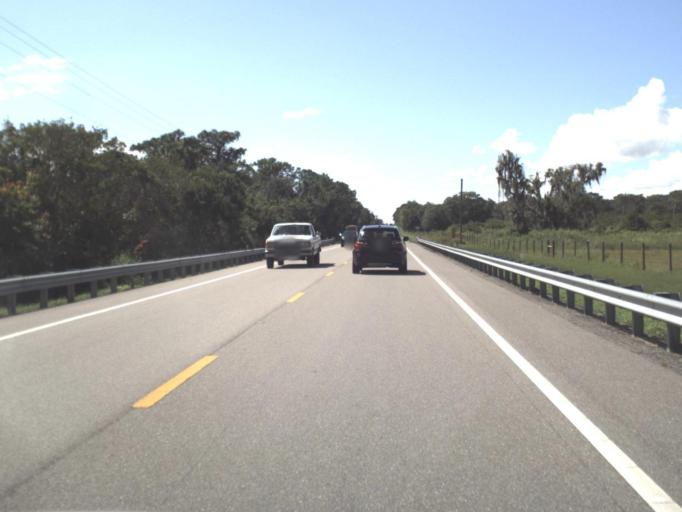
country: US
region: Florida
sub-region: Sarasota County
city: Lake Sarasota
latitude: 27.3872
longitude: -82.2575
